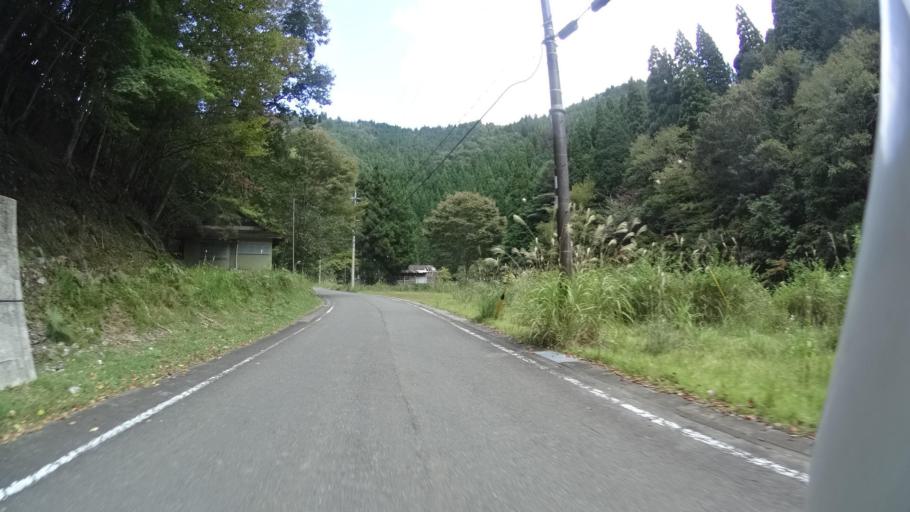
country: JP
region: Fukui
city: Obama
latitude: 35.2859
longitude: 135.6980
